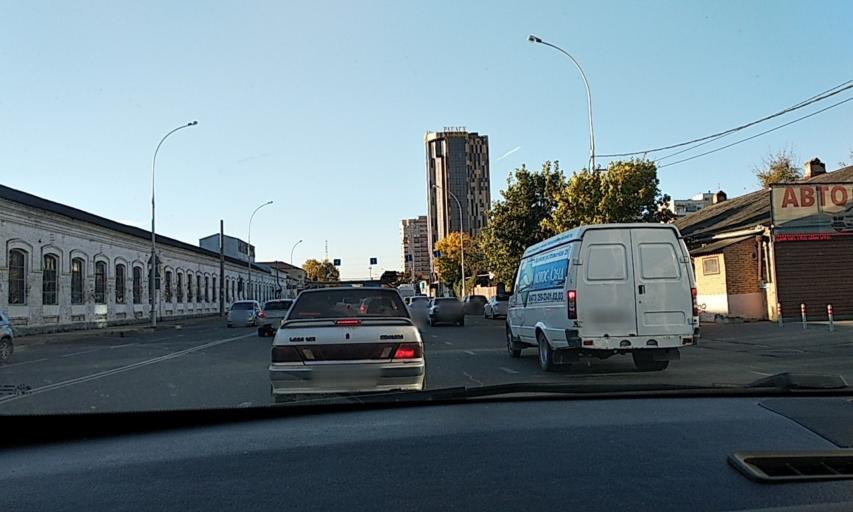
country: RU
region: Krasnodarskiy
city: Krasnodar
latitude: 45.0204
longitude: 38.9813
